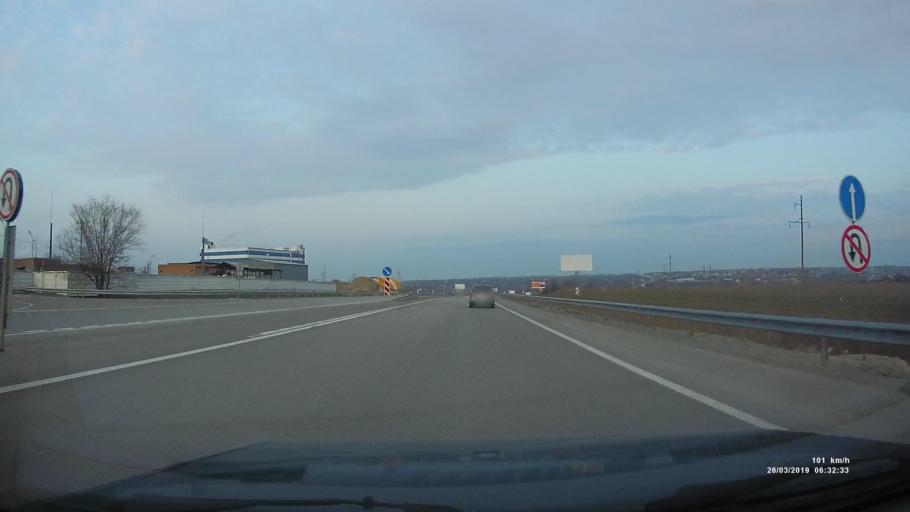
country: RU
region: Rostov
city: Kalinin
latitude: 47.2701
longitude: 39.5075
